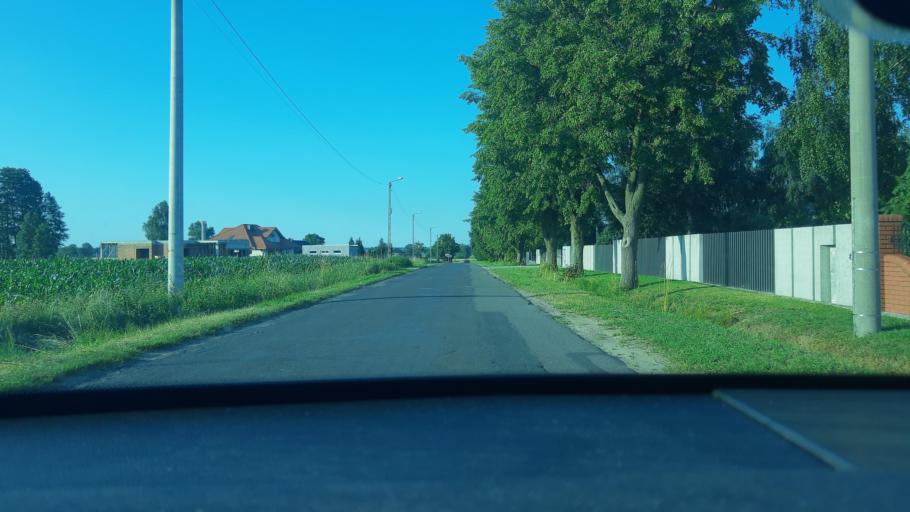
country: PL
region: Lodz Voivodeship
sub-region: Powiat sieradzki
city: Sieradz
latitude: 51.5518
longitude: 18.7602
